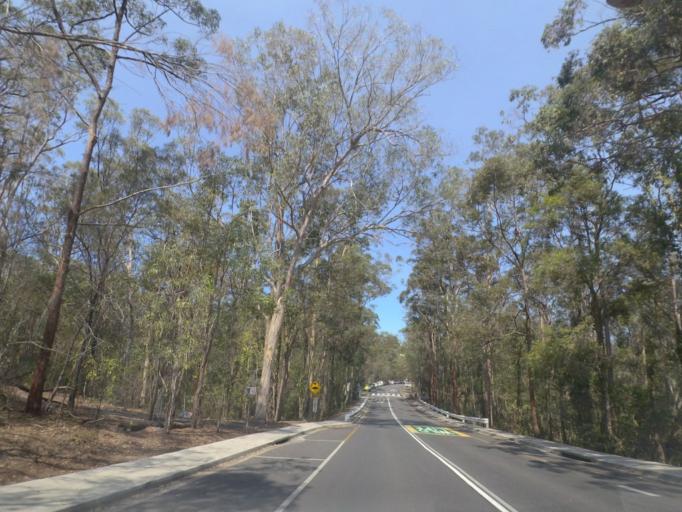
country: AU
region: Queensland
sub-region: Brisbane
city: Nathan
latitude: -27.5504
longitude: 153.0593
